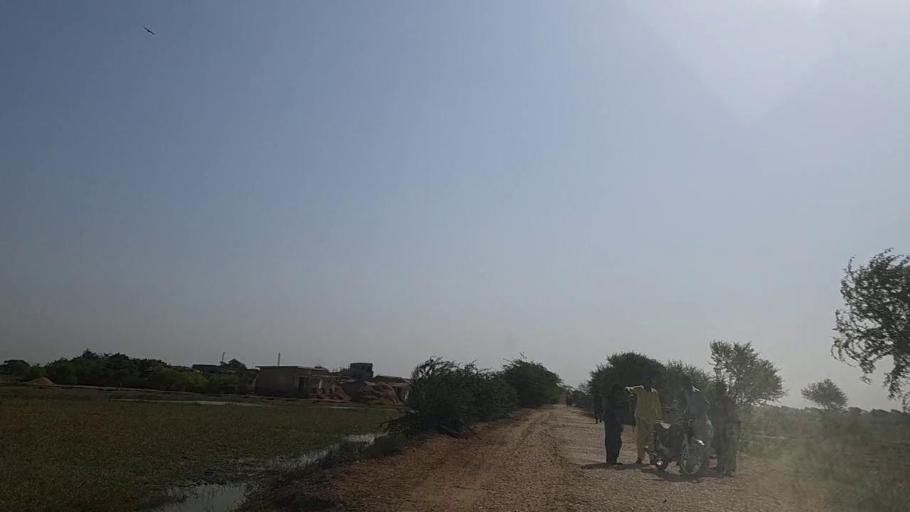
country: PK
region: Sindh
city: Daro Mehar
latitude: 24.7201
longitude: 68.0777
